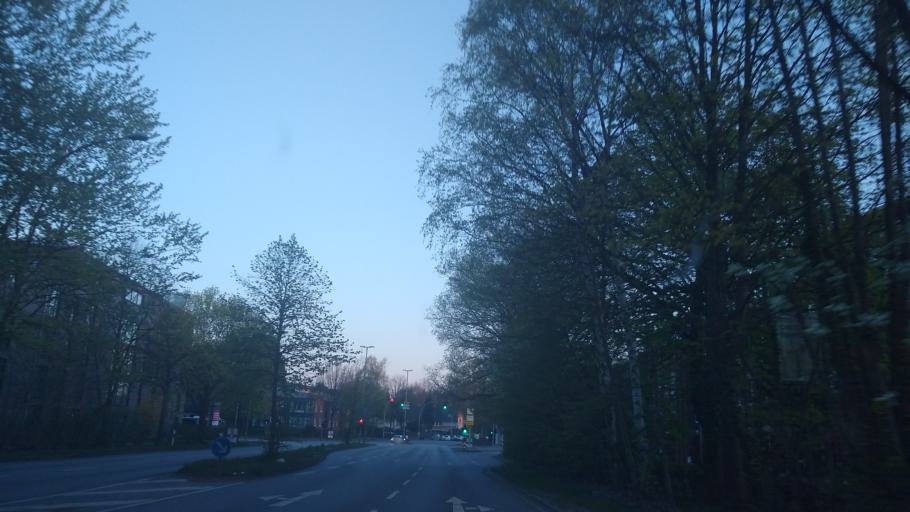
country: DE
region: Schleswig-Holstein
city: Bonningstedt
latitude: 53.6366
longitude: 9.9209
